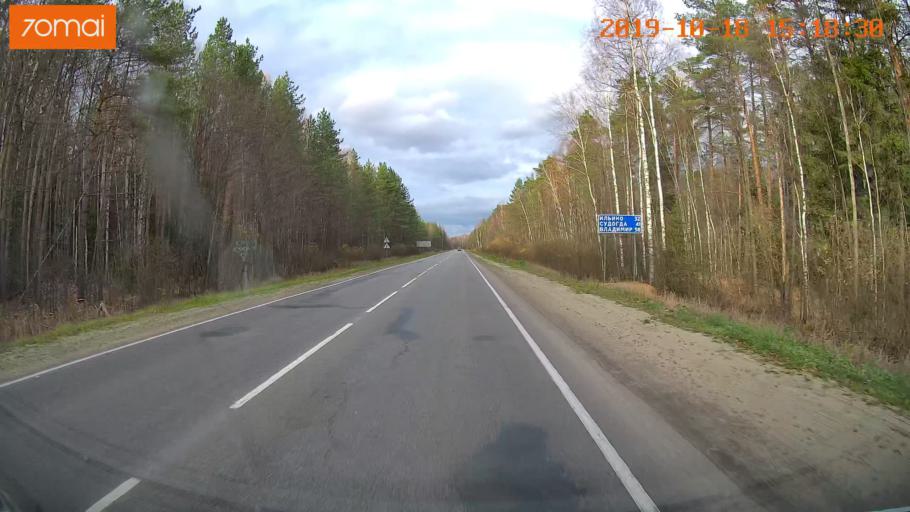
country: RU
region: Vladimir
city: Anopino
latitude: 55.6601
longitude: 40.7294
